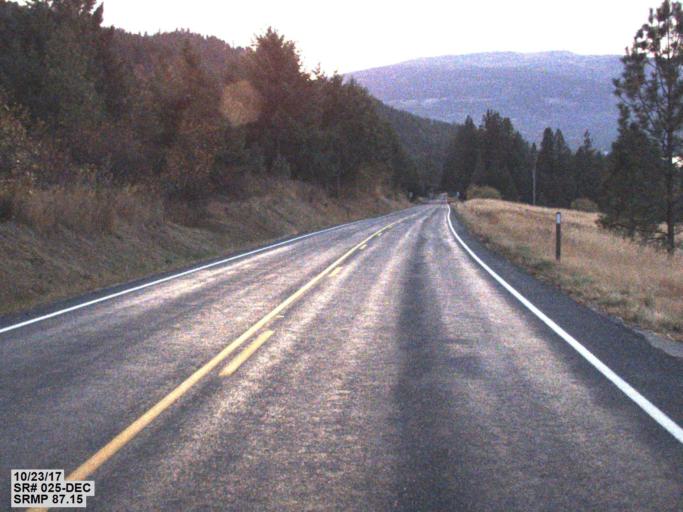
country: US
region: Washington
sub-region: Stevens County
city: Kettle Falls
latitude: 48.6682
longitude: -118.0427
